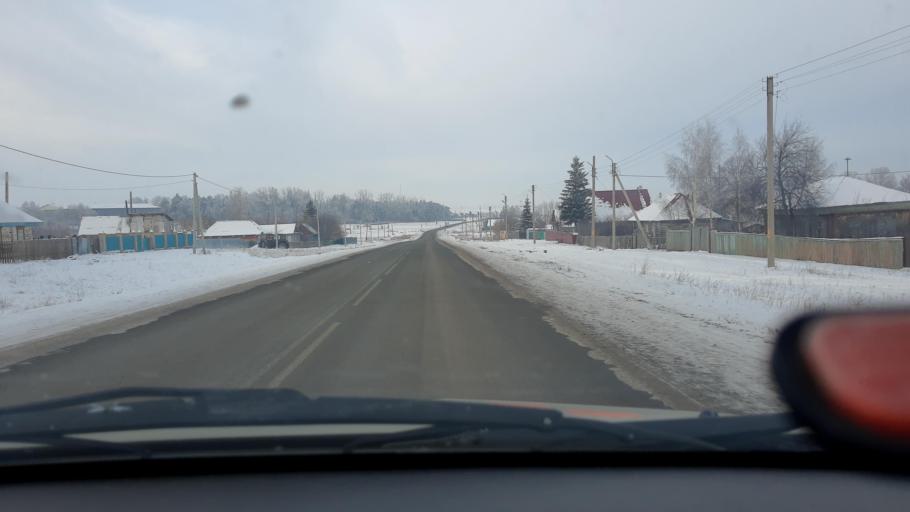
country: RU
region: Bashkortostan
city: Avdon
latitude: 54.3738
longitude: 55.8135
